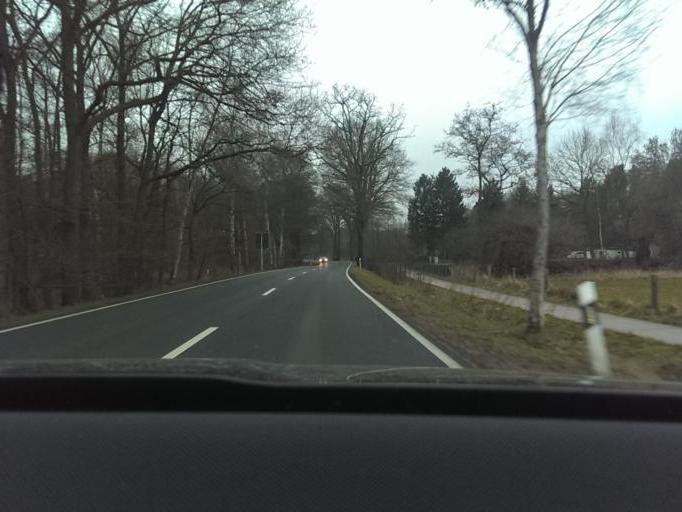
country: DE
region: Lower Saxony
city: Isernhagen Farster Bauerschaft
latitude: 52.5144
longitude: 9.8029
